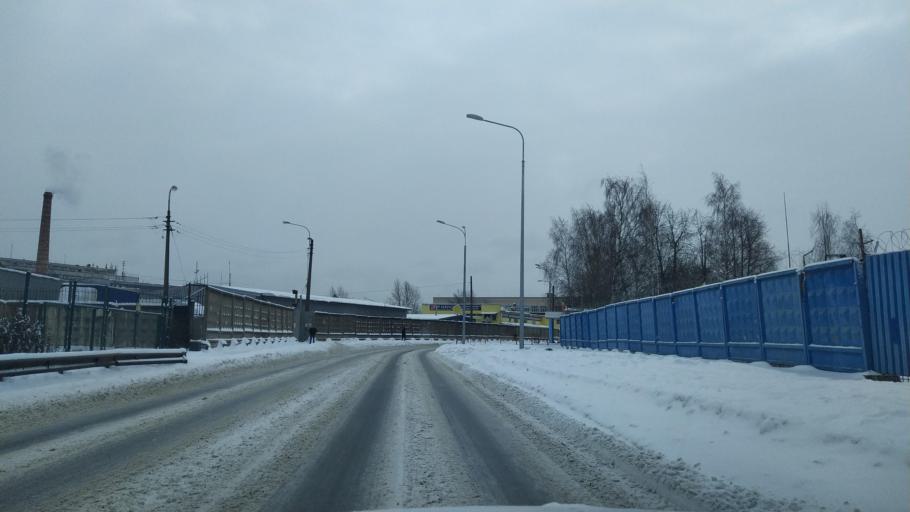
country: RU
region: St.-Petersburg
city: Novaya Derevnya
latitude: 59.9917
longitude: 30.2774
